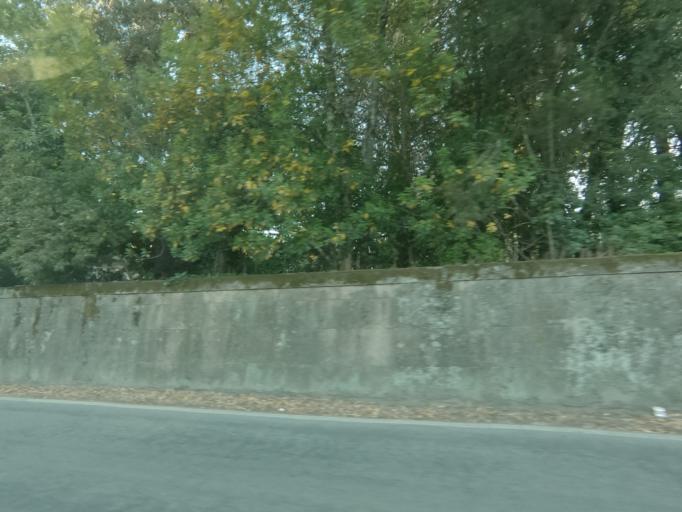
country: PT
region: Vila Real
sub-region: Vila Real
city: Vila Real
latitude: 41.2974
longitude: -7.7127
